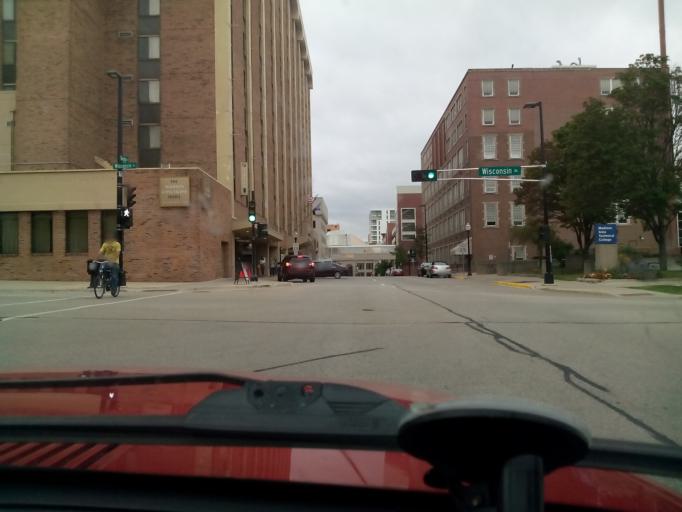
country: US
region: Wisconsin
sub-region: Dane County
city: Madison
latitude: 43.0763
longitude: -89.3860
